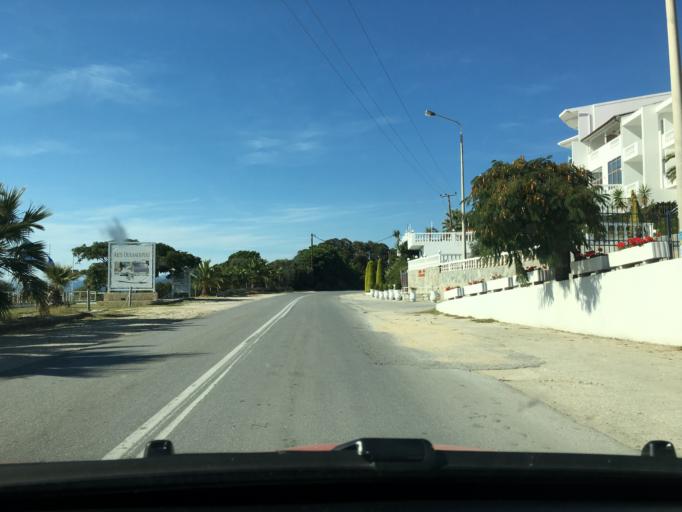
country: GR
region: Central Macedonia
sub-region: Nomos Chalkidikis
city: Ouranoupolis
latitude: 40.3470
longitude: 23.9637
